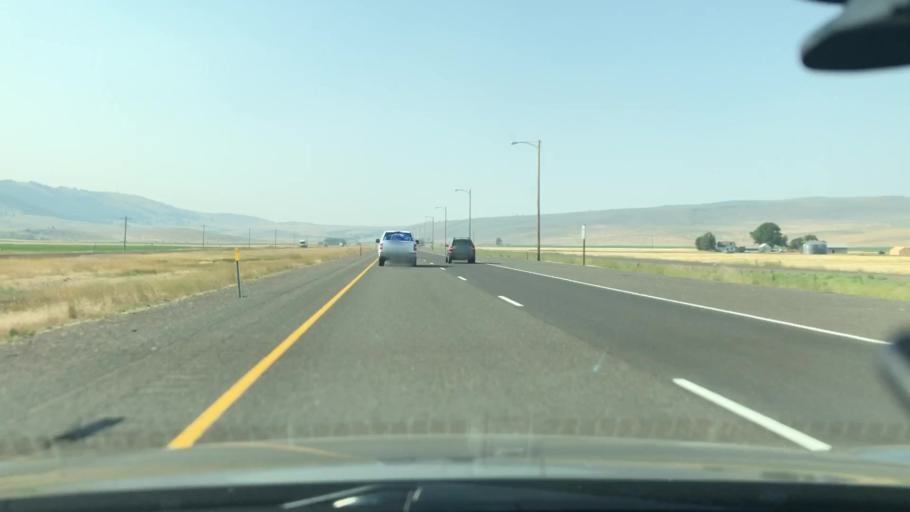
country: US
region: Oregon
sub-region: Union County
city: Union
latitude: 45.1000
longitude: -117.9539
